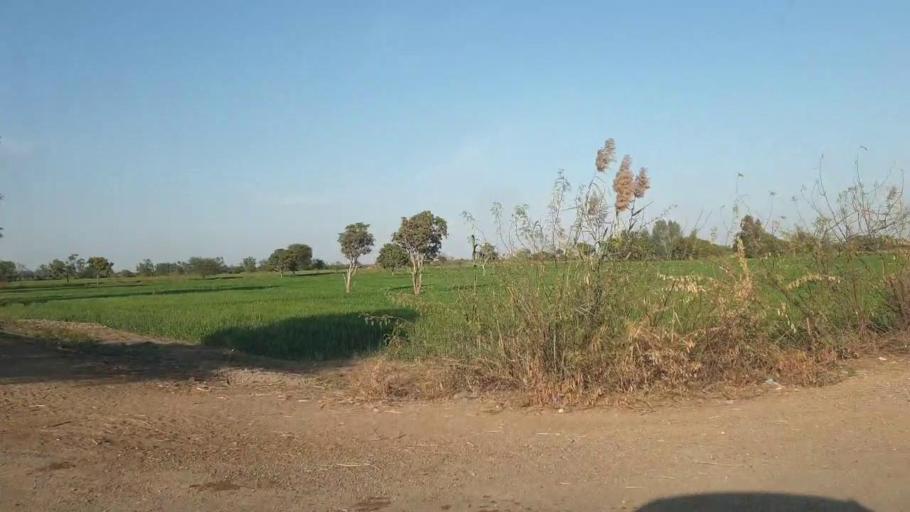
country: PK
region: Sindh
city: Chambar
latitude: 25.2886
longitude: 68.7477
